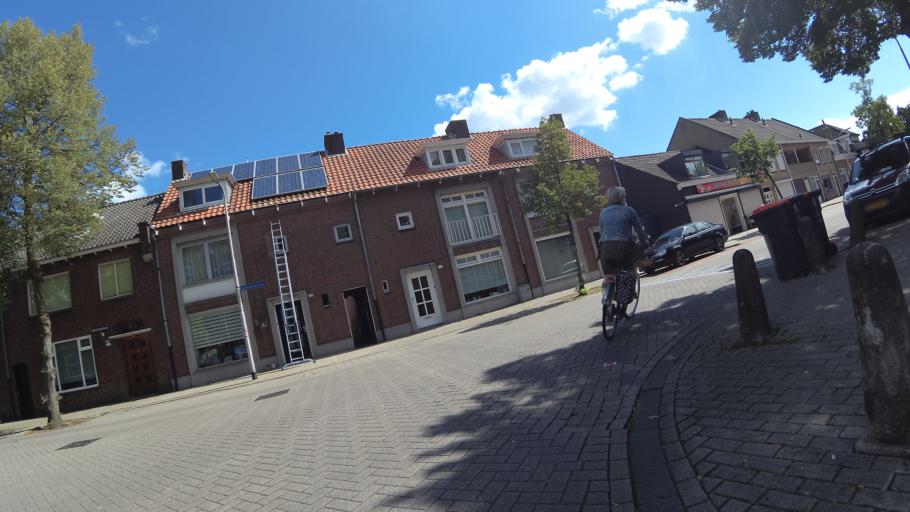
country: NL
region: North Brabant
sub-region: Gemeente Goirle
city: Goirle
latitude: 51.5498
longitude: 5.0616
